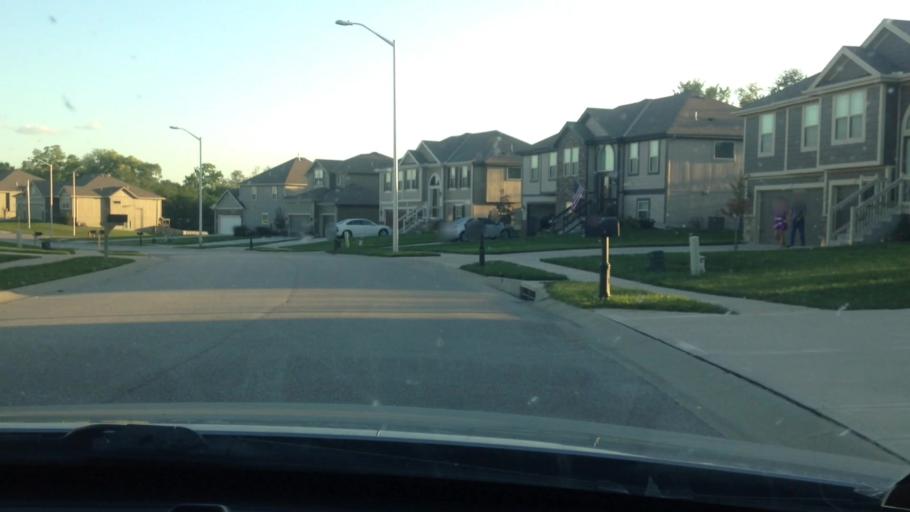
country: US
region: Missouri
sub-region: Clay County
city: Smithville
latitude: 39.2960
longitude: -94.5888
